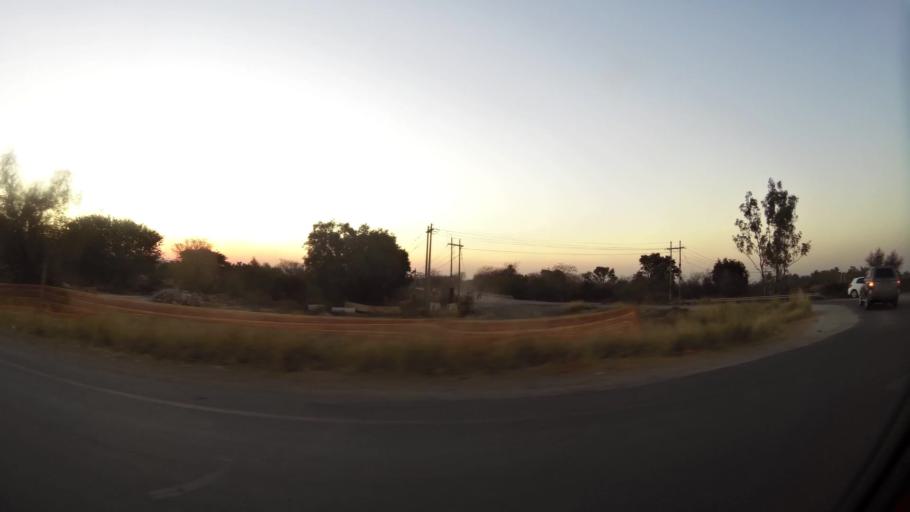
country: ZA
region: North-West
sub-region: Bojanala Platinum District Municipality
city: Rustenburg
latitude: -25.6483
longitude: 27.2540
